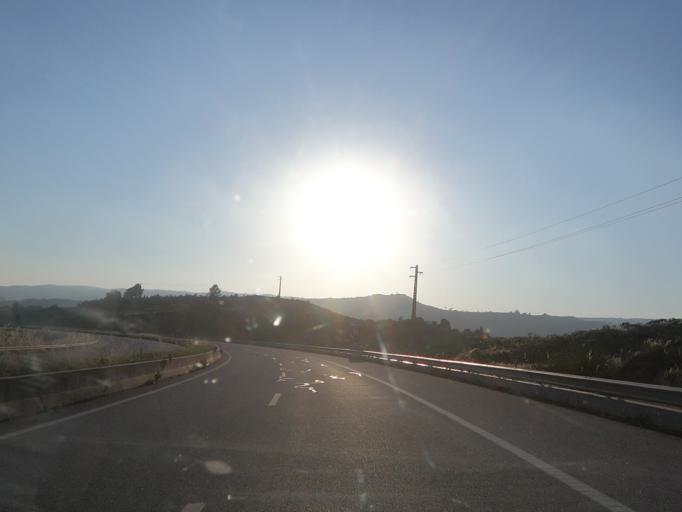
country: PT
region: Guarda
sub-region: Celorico da Beira
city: Celorico da Beira
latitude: 40.6355
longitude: -7.4546
